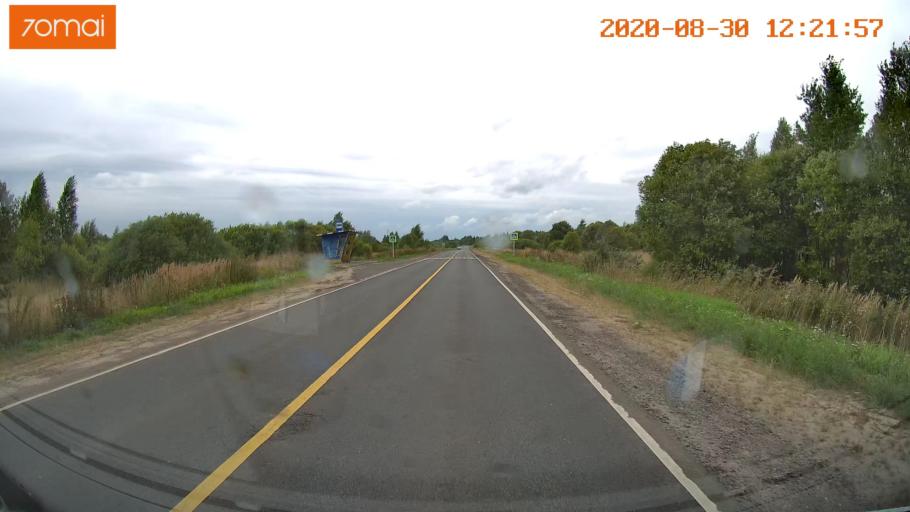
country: RU
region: Ivanovo
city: Yur'yevets
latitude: 57.3274
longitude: 42.8628
